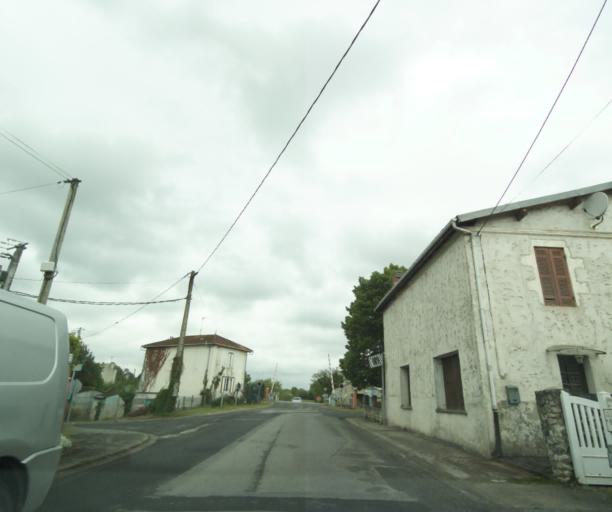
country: FR
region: Poitou-Charentes
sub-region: Departement de la Charente-Maritime
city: Chaniers
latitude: 45.6964
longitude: -0.5273
